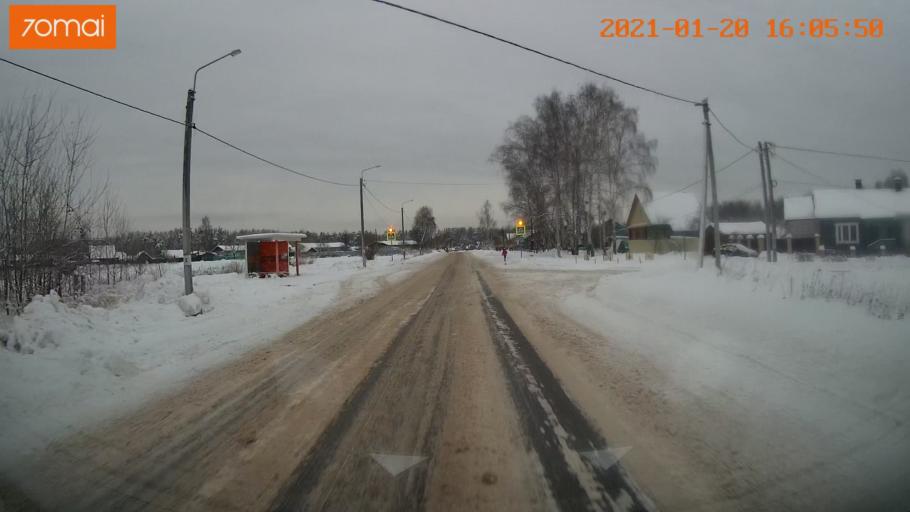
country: RU
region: Vladimir
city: Sudogda
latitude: 56.0678
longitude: 40.8001
